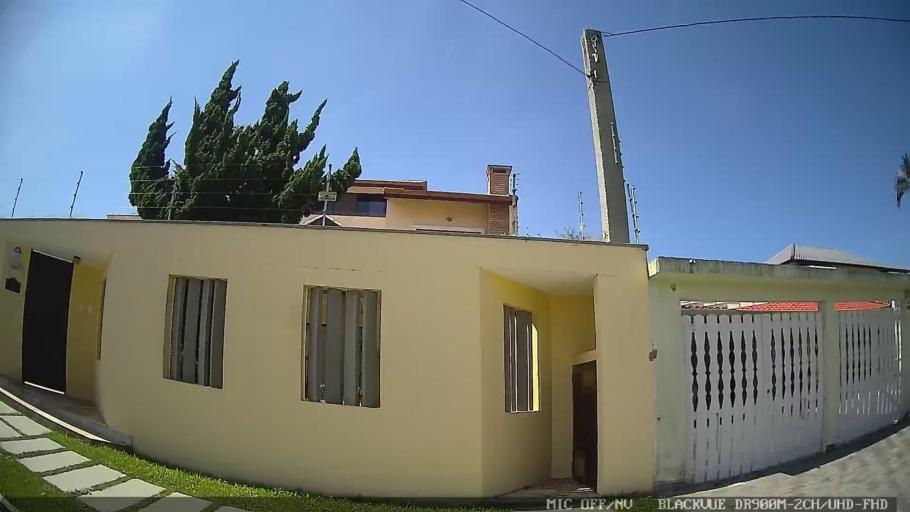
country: BR
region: Sao Paulo
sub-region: Peruibe
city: Peruibe
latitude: -24.2946
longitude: -46.9688
